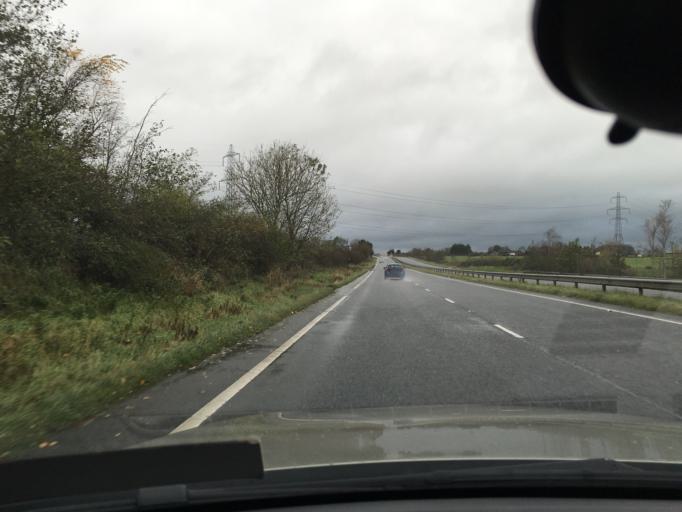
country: GB
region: Northern Ireland
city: Carnmoney
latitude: 54.7166
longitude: -5.9685
